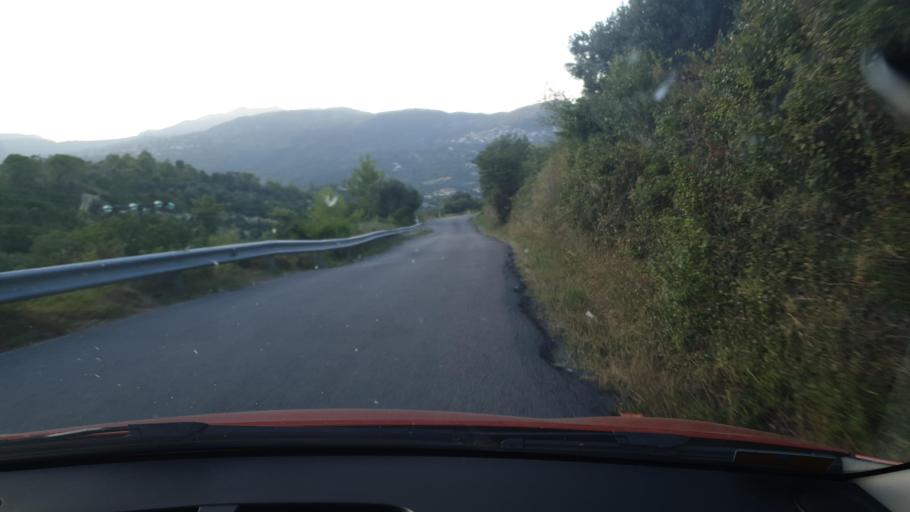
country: GR
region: Central Greece
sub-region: Nomos Evvoias
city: Oxilithos
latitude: 38.5952
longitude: 24.1174
